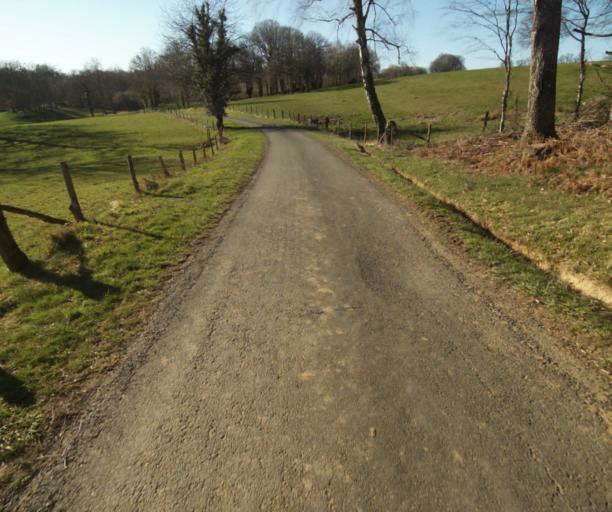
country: FR
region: Limousin
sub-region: Departement de la Correze
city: Seilhac
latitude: 45.3856
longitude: 1.6951
